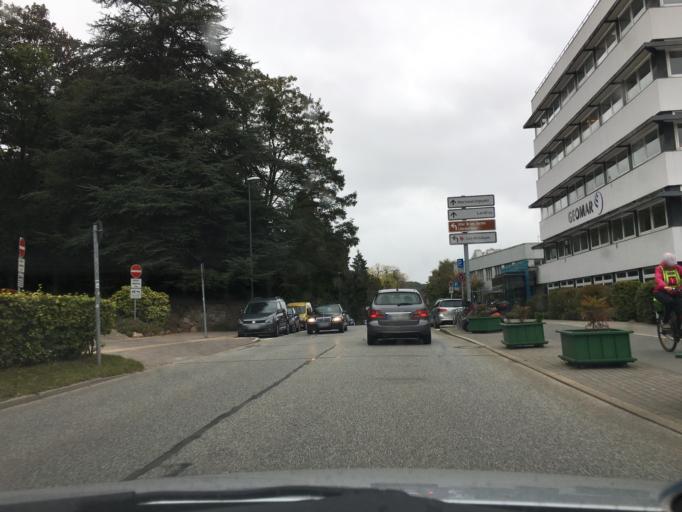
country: DE
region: Schleswig-Holstein
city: Kiel
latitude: 54.3296
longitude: 10.1476
